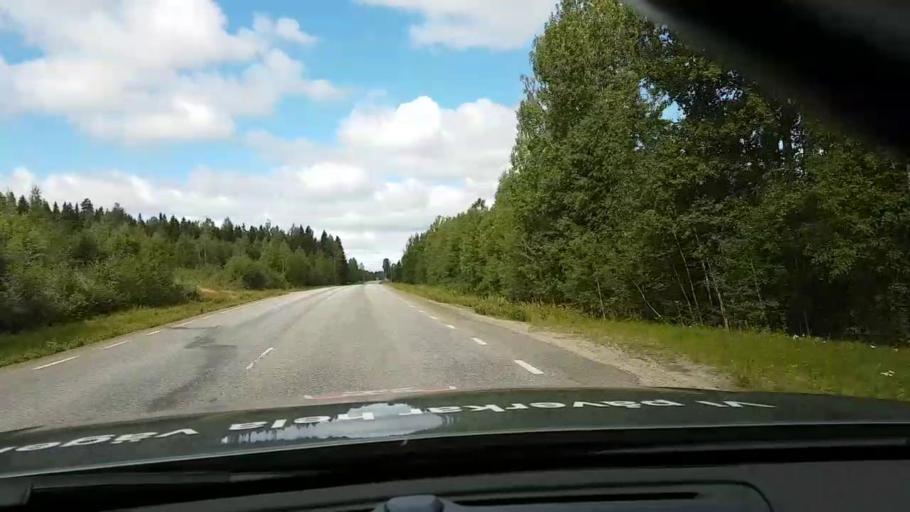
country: SE
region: Vaesternorrland
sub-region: OErnskoeldsviks Kommun
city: Bredbyn
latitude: 63.4725
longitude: 18.0980
